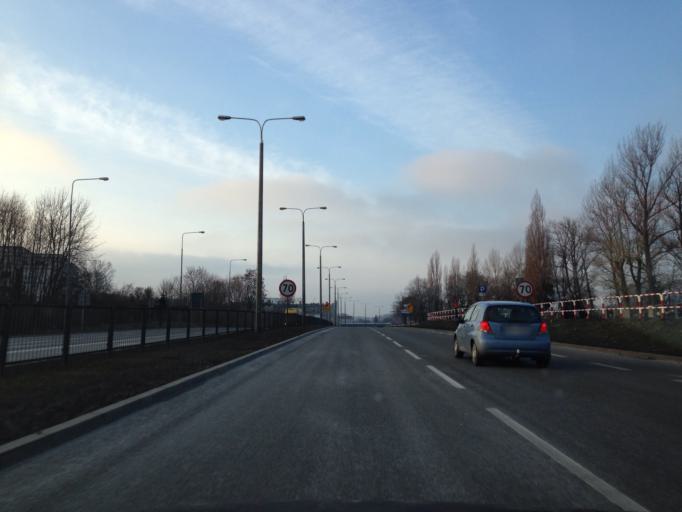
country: PL
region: Greater Poland Voivodeship
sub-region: Powiat gnieznienski
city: Gniezno
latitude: 52.5434
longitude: 17.6006
